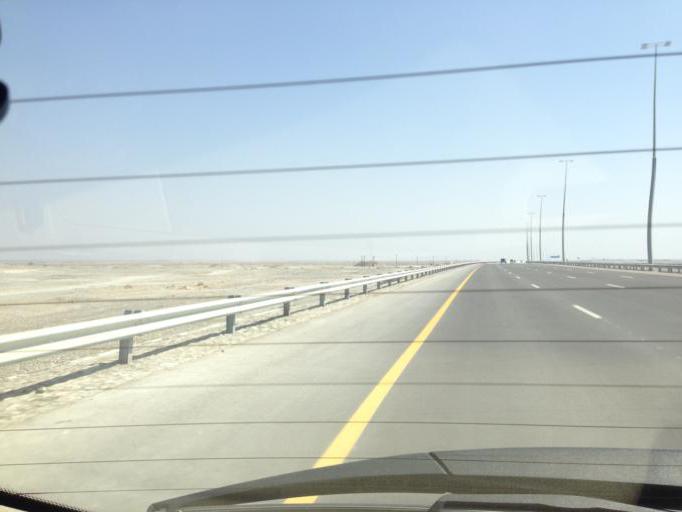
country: OM
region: Al Batinah
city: Barka'
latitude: 23.5624
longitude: 57.6992
